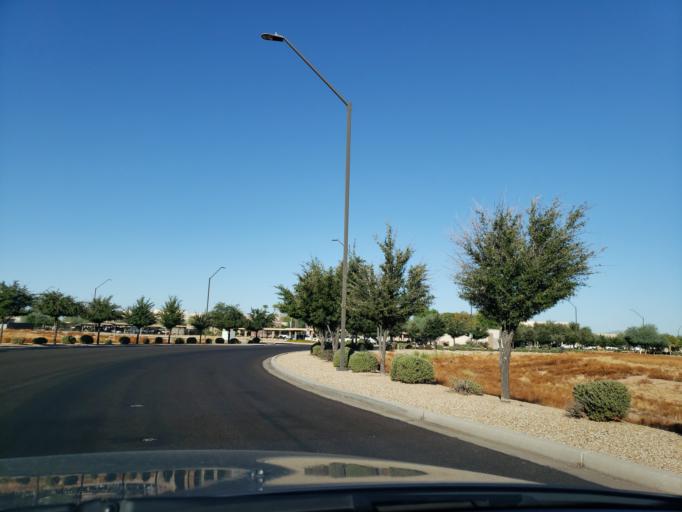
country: US
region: Arizona
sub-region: Maricopa County
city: Tolleson
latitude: 33.4438
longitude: -112.3017
